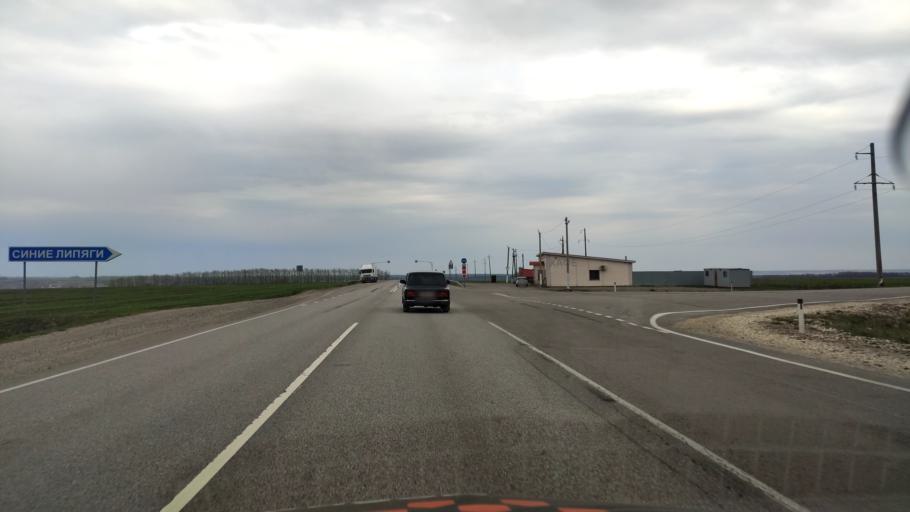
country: RU
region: Voronezj
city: Nizhnedevitsk
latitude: 51.5845
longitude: 38.5379
